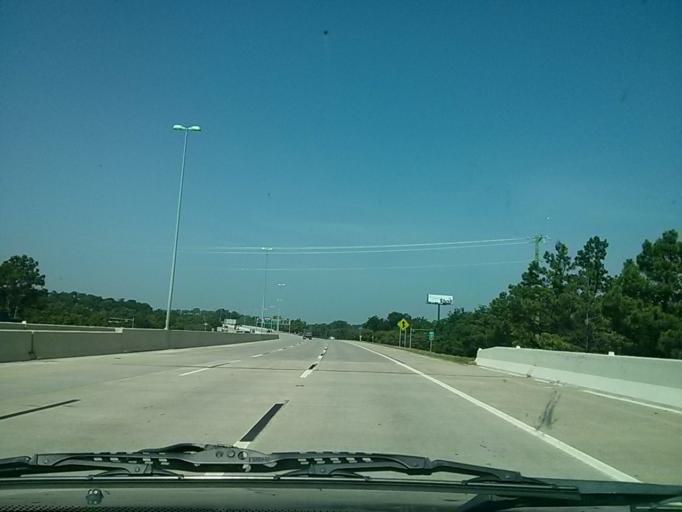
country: US
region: Oklahoma
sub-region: Tulsa County
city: Jenks
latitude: 36.0168
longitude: -95.9759
